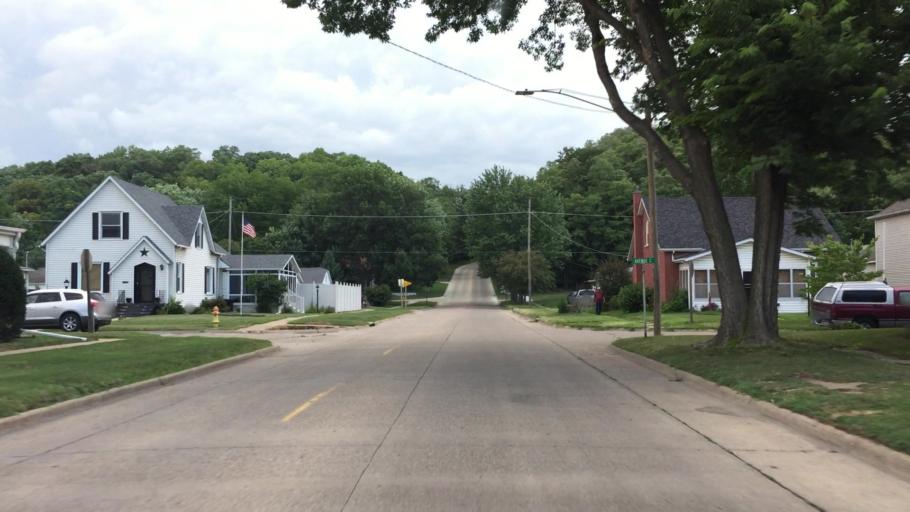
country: US
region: Iowa
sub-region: Lee County
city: Fort Madison
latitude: 40.6350
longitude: -91.3245
